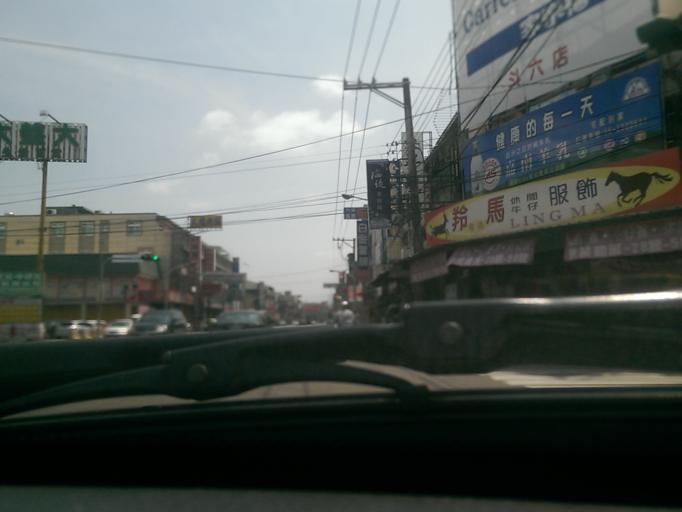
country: TW
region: Taiwan
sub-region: Yunlin
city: Douliu
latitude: 23.7004
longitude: 120.4257
